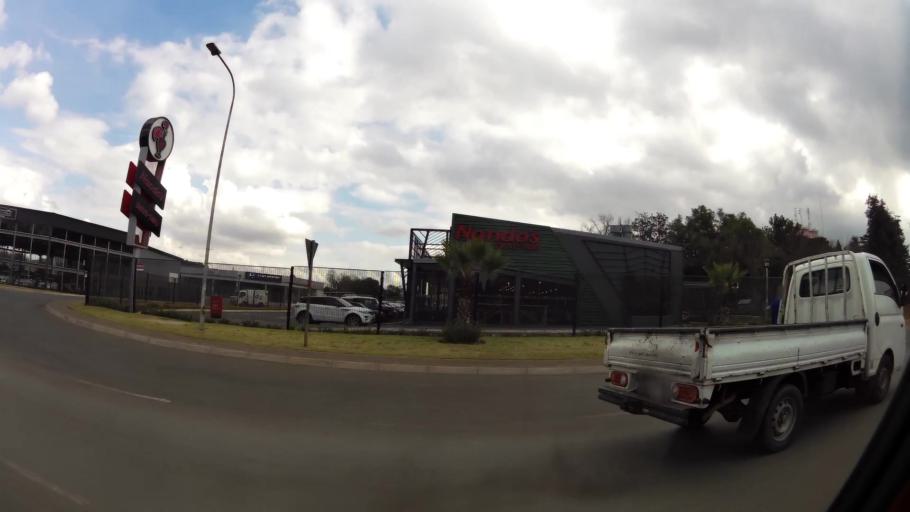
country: ZA
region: Gauteng
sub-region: Sedibeng District Municipality
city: Vanderbijlpark
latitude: -26.7046
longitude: 27.8357
